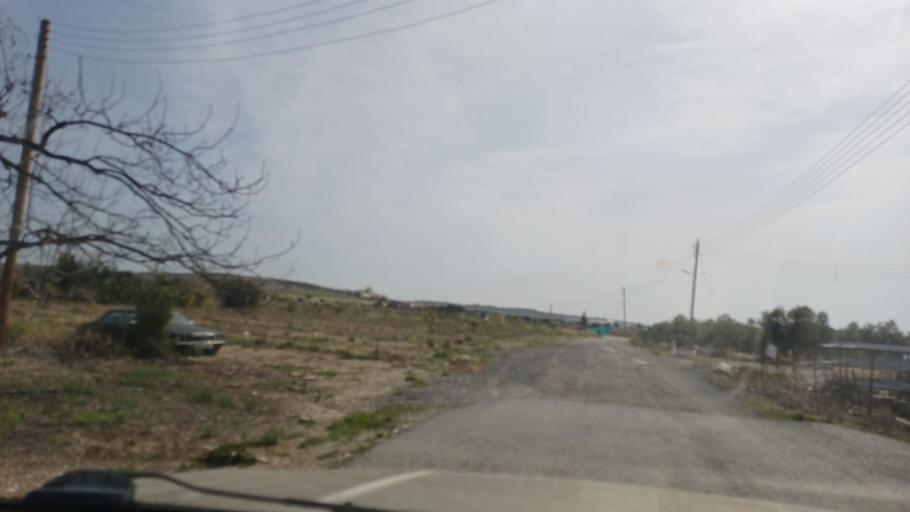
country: CY
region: Pafos
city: Paphos
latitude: 34.7538
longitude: 32.4732
